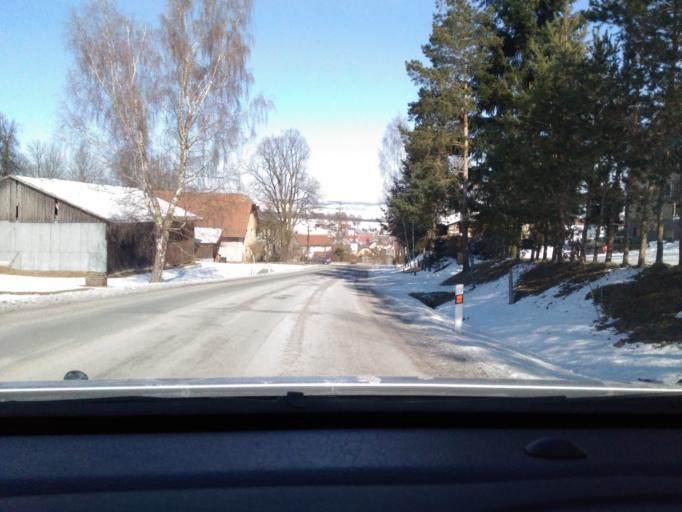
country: CZ
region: Vysocina
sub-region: Okres Zd'ar nad Sazavou
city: Nove Mesto na Morave
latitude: 49.5256
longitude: 16.0362
